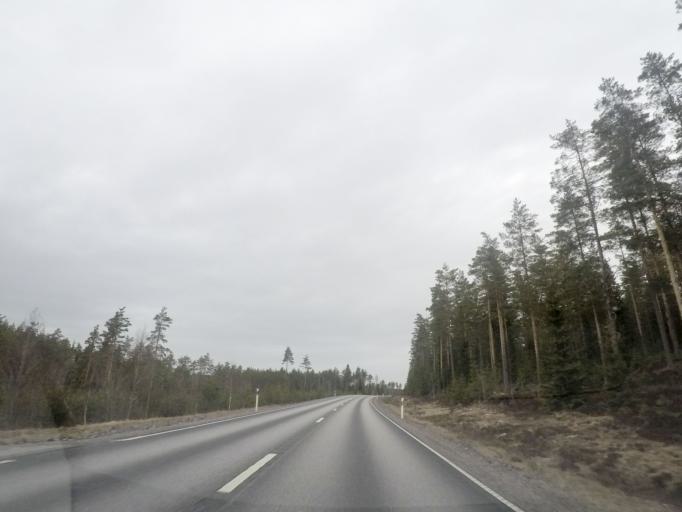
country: SE
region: OErebro
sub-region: Ljusnarsbergs Kommun
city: Kopparberg
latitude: 59.9472
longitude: 15.0218
